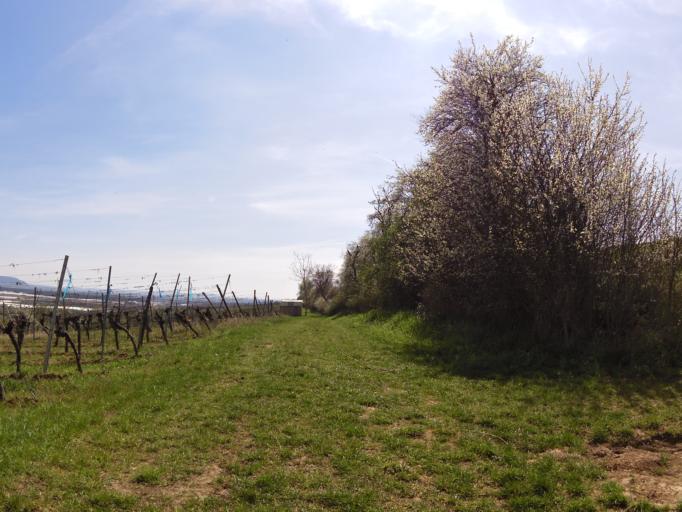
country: DE
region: Bavaria
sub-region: Regierungsbezirk Unterfranken
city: Mainstockheim
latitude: 49.7984
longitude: 10.1491
